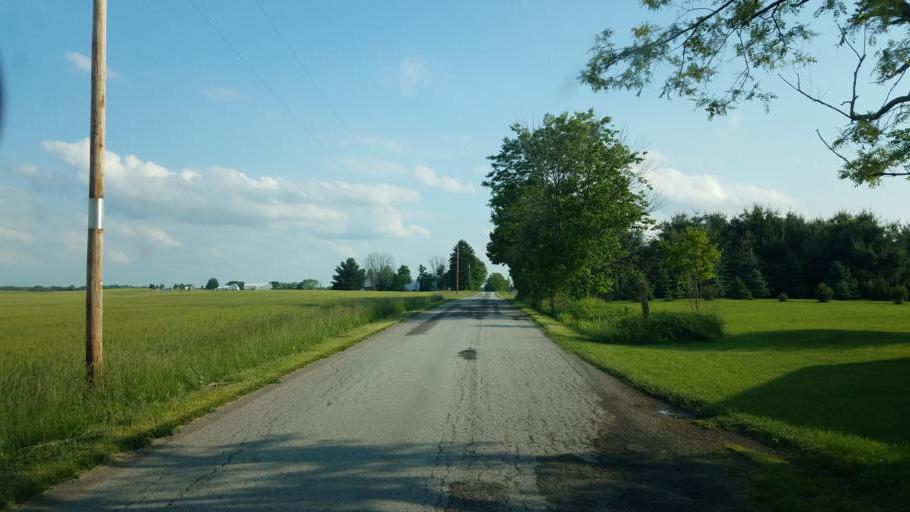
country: US
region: Ohio
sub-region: Knox County
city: Centerburg
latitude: 40.3847
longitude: -82.7991
